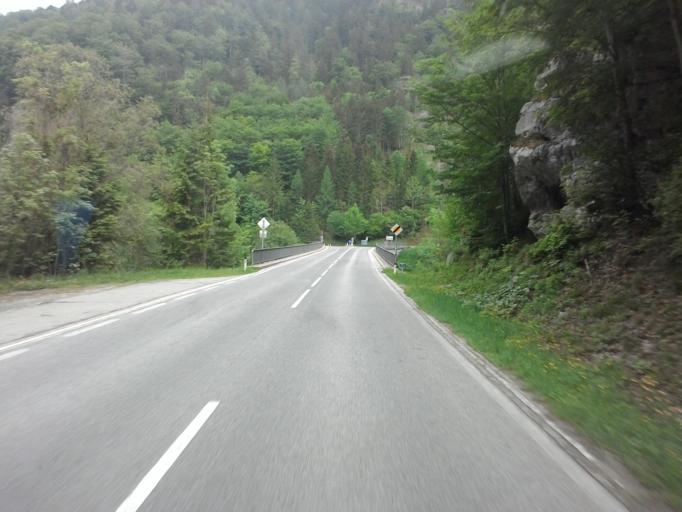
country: AT
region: Styria
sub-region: Politischer Bezirk Liezen
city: Palfau
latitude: 47.7124
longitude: 14.8322
